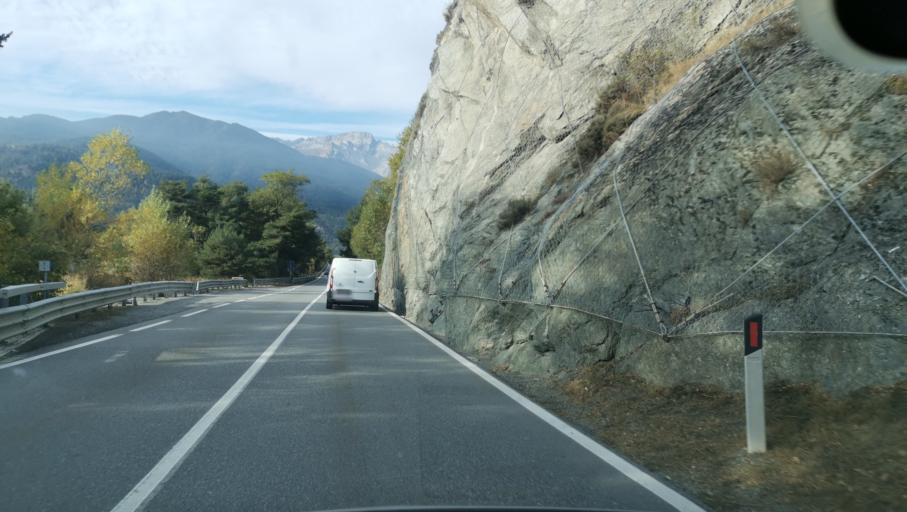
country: IT
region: Piedmont
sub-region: Provincia di Torino
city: Oulx
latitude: 45.0474
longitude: 6.8392
